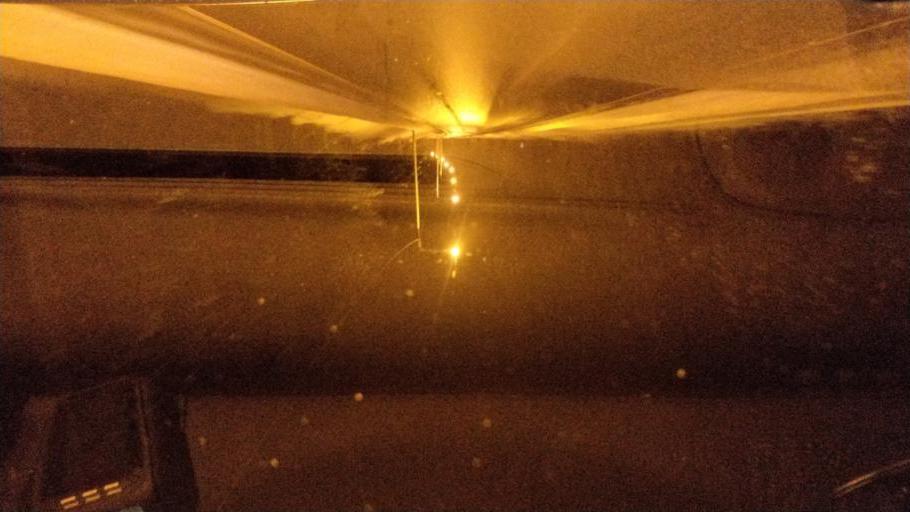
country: FI
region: Lapland
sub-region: Kemi-Tornio
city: Tervola
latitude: 66.1365
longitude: 24.9299
